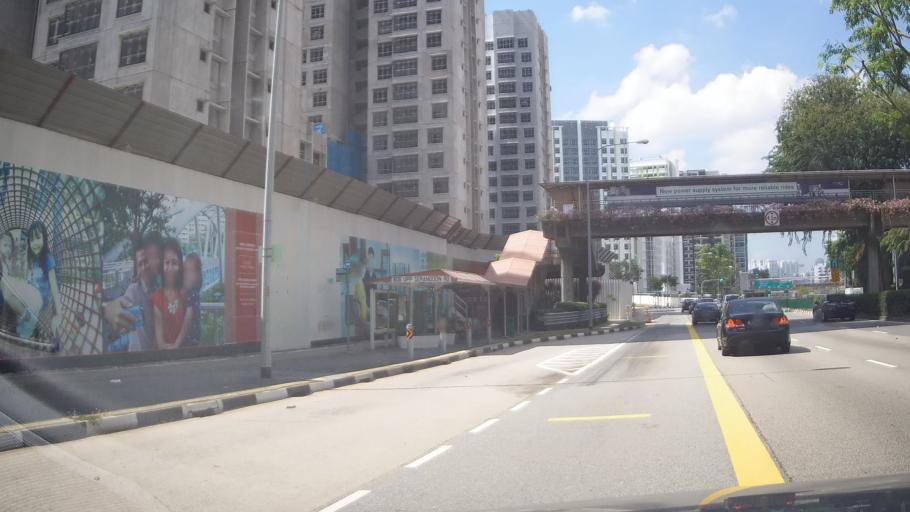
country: SG
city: Singapore
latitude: 1.3364
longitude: 103.8707
